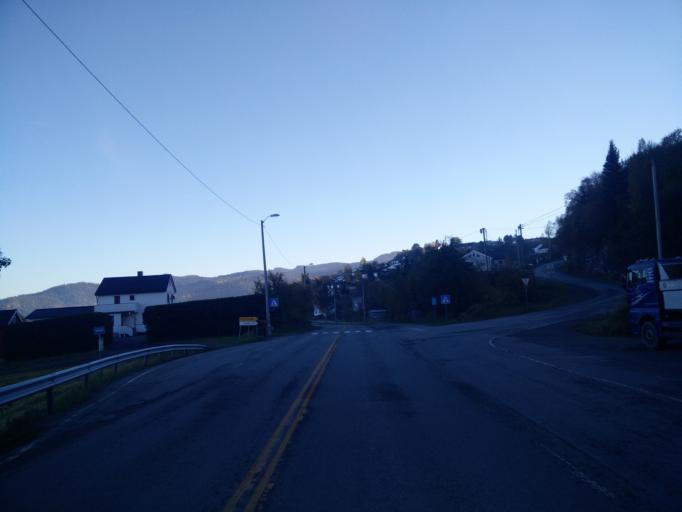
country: NO
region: Sor-Trondelag
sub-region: Skaun
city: Borsa
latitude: 63.3379
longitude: 10.0595
